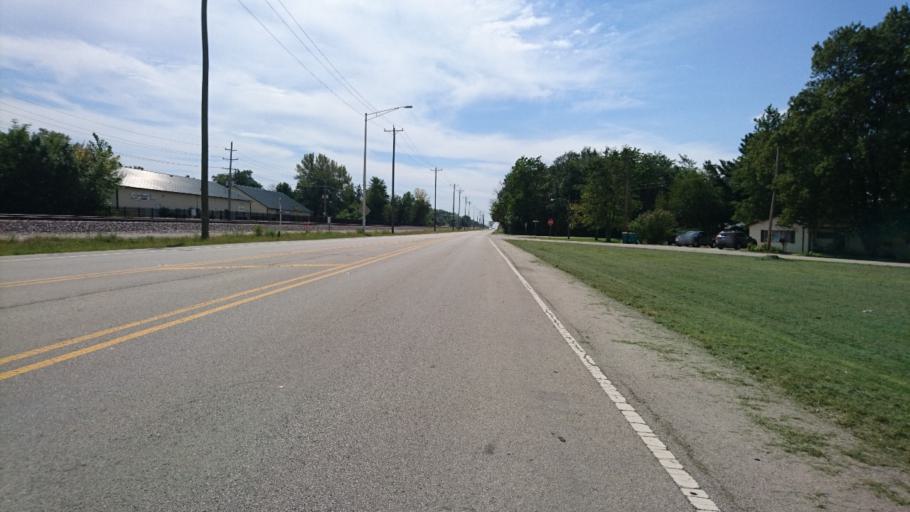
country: US
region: Illinois
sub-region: Will County
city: Braidwood
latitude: 41.2636
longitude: -88.2132
